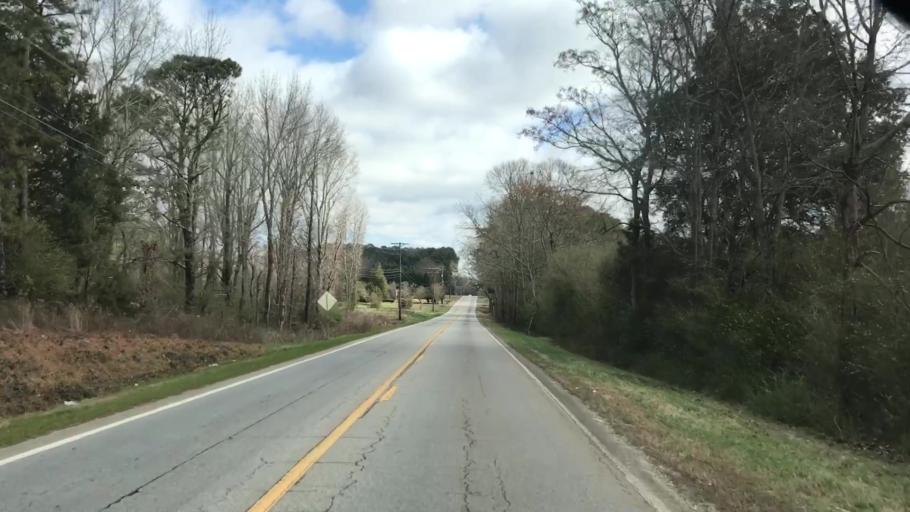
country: US
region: Georgia
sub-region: Barrow County
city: Russell
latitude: 33.9744
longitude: -83.6747
